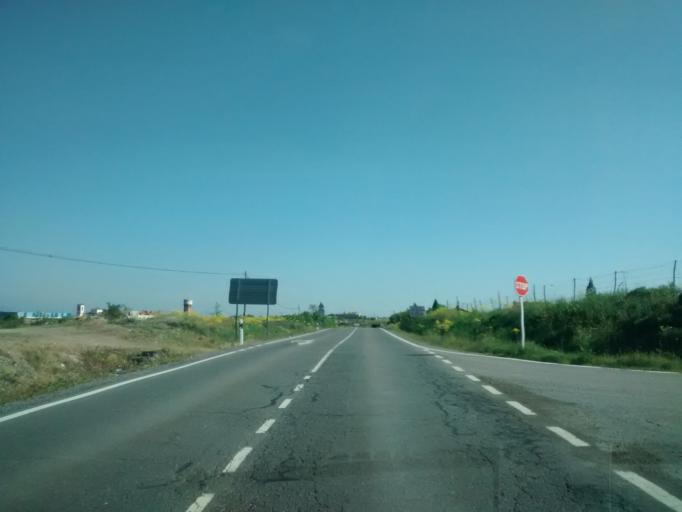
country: ES
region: Castille and Leon
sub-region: Provincia de Segovia
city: Trescasas
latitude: 40.9512
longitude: -4.0339
